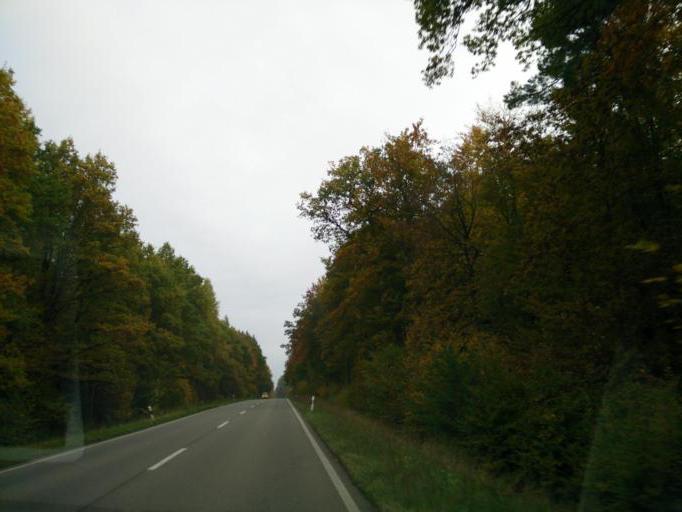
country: DE
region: Baden-Wuerttemberg
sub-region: Tuebingen Region
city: Dettenhausen
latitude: 48.5857
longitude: 9.1059
